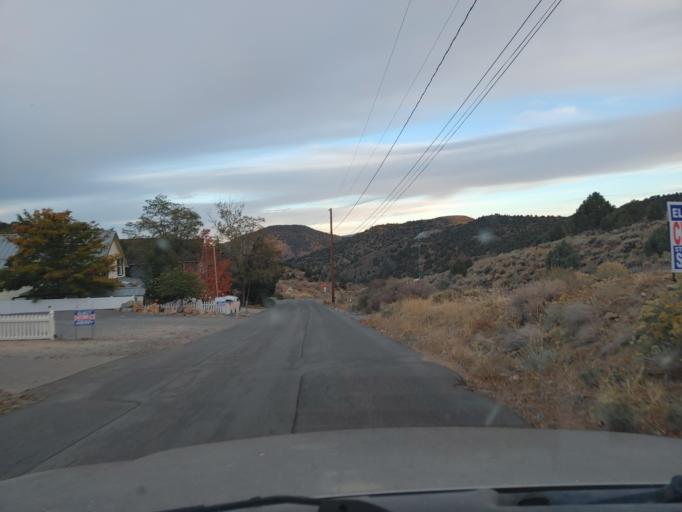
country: US
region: Nevada
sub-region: Storey County
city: Virginia City
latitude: 39.3113
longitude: -119.6416
